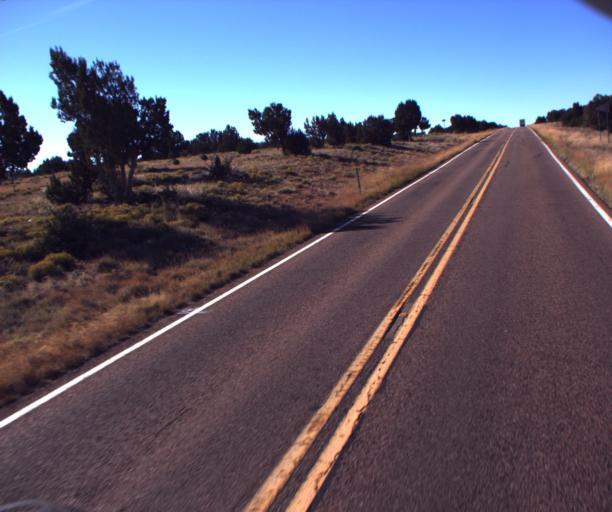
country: US
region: Arizona
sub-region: Navajo County
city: Heber-Overgaard
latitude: 34.5023
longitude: -110.4521
